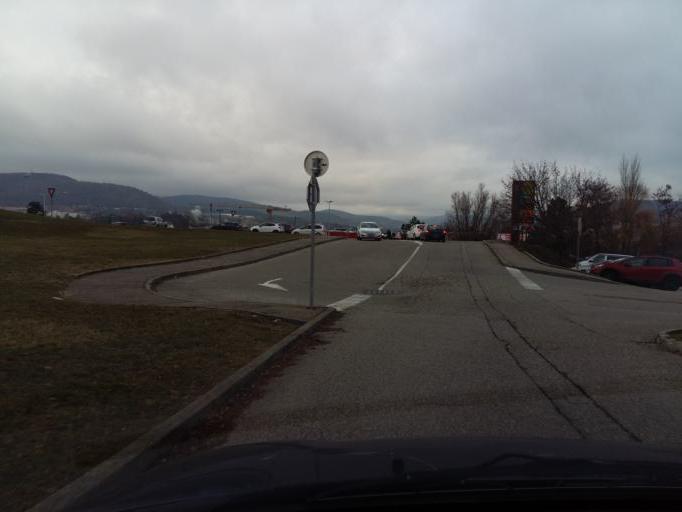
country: FR
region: Rhone-Alpes
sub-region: Departement de l'Ardeche
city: Davezieux
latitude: 45.2547
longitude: 4.6887
